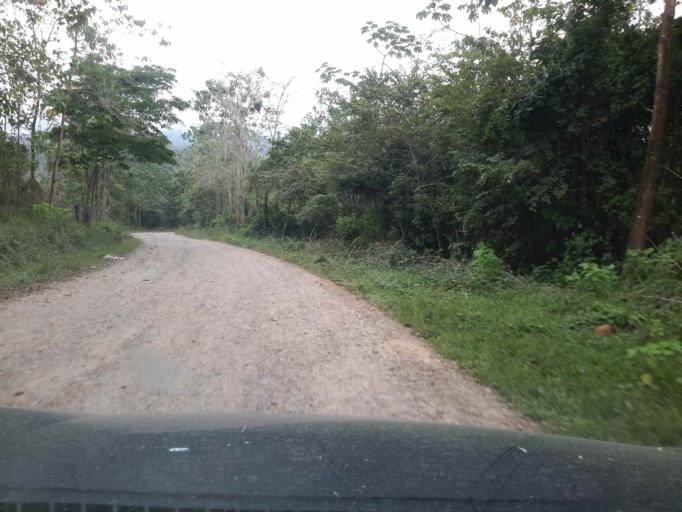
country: CR
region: Alajuela
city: Los Chiles
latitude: 11.1055
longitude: -84.5824
